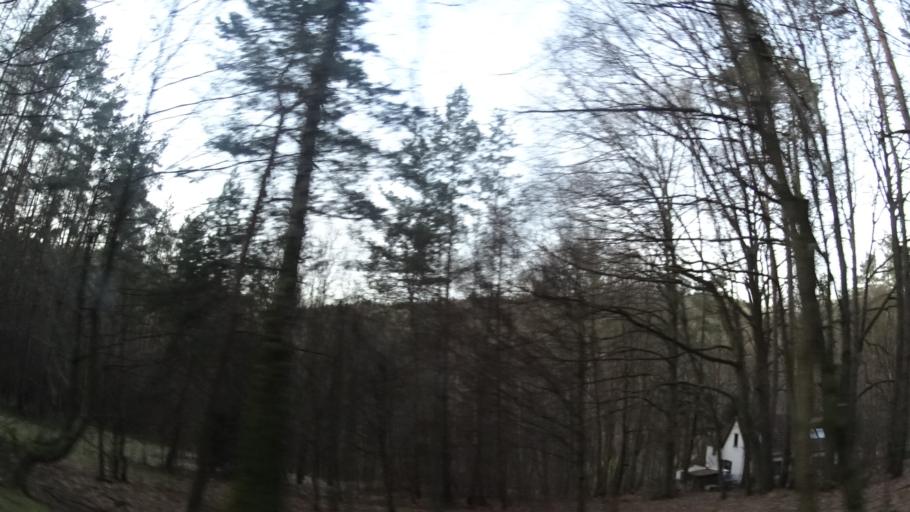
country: DE
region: Bavaria
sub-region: Regierungsbezirk Unterfranken
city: Mombris
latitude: 50.0899
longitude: 9.1671
